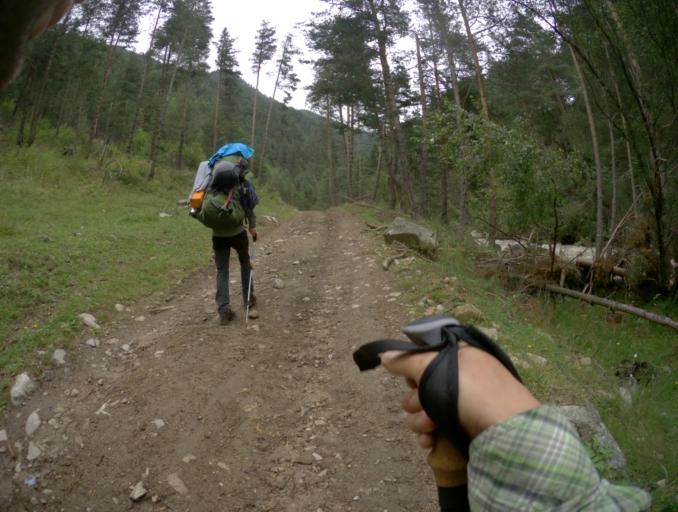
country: RU
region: Karachayevo-Cherkesiya
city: Uchkulan
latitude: 43.4189
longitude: 42.2161
